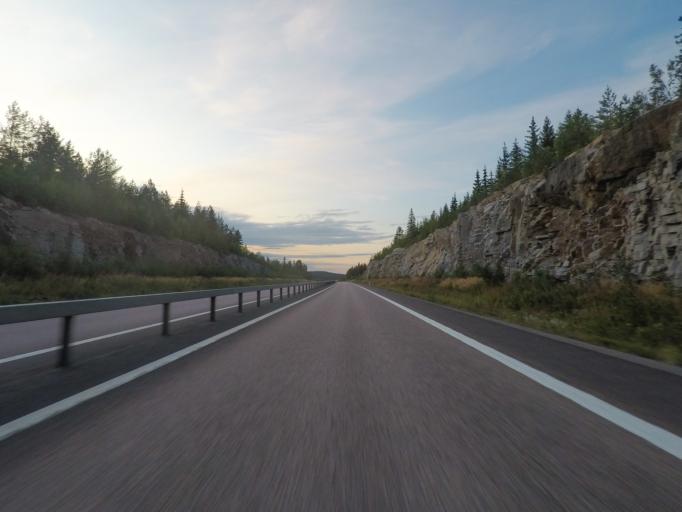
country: FI
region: Central Finland
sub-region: Jyvaeskylae
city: Saeynaetsalo
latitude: 62.1811
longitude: 25.9064
